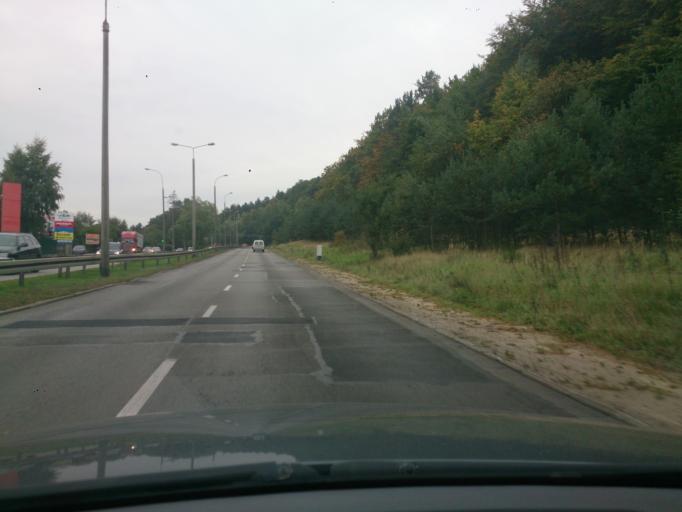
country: PL
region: Pomeranian Voivodeship
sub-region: Powiat wejherowski
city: Rumia
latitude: 54.5560
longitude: 18.4094
